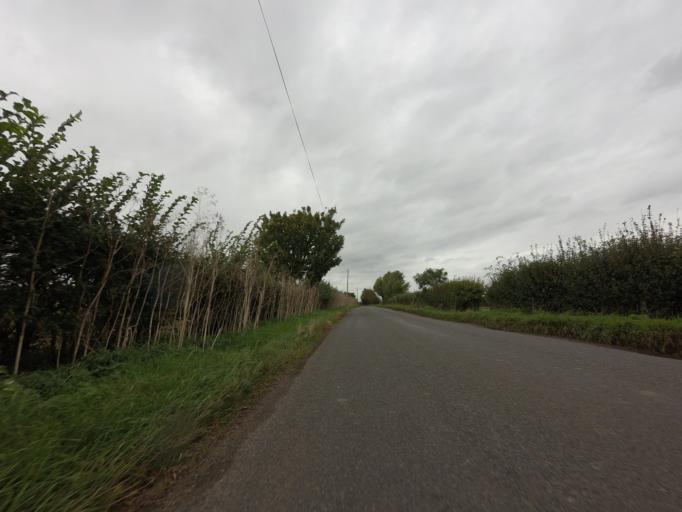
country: GB
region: England
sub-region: Cambridgeshire
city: Harston
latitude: 52.1024
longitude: 0.0558
